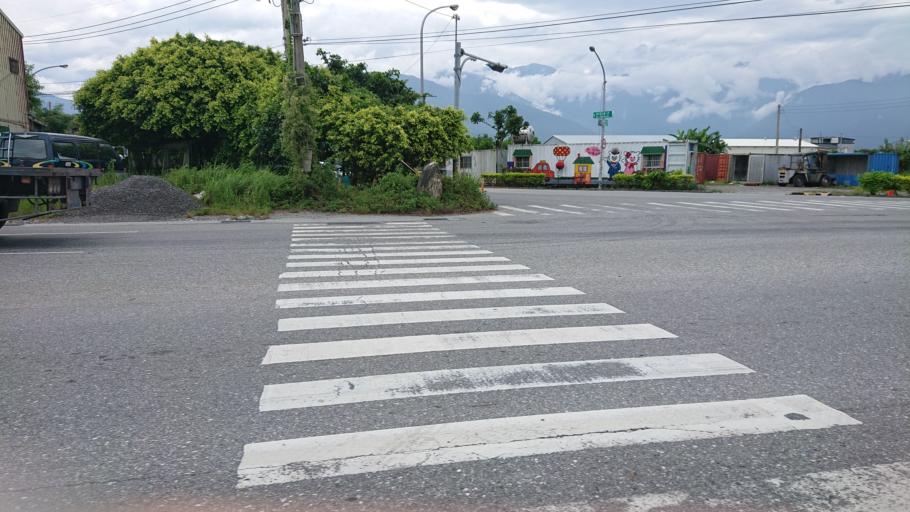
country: TW
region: Taiwan
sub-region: Hualien
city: Hualian
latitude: 23.9414
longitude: 121.5950
